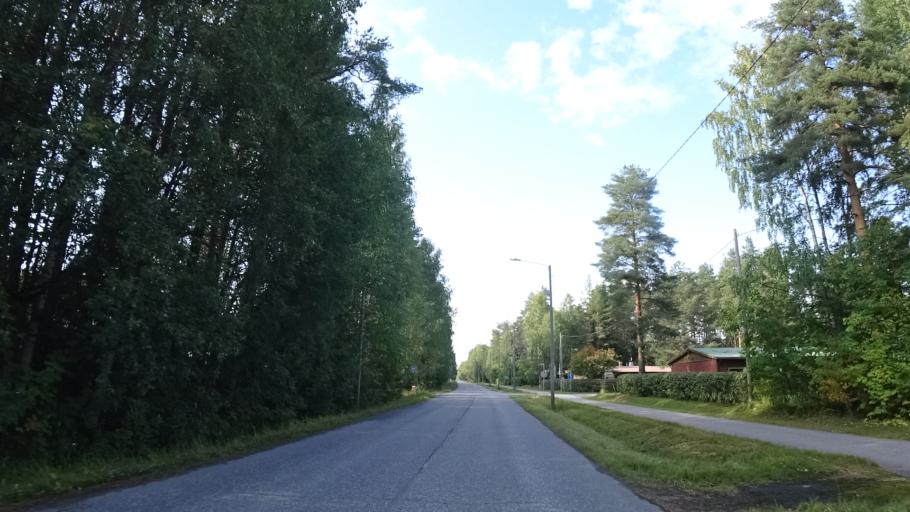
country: FI
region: North Karelia
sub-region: Pielisen Karjala
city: Lieksa
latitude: 63.3336
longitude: 30.0292
